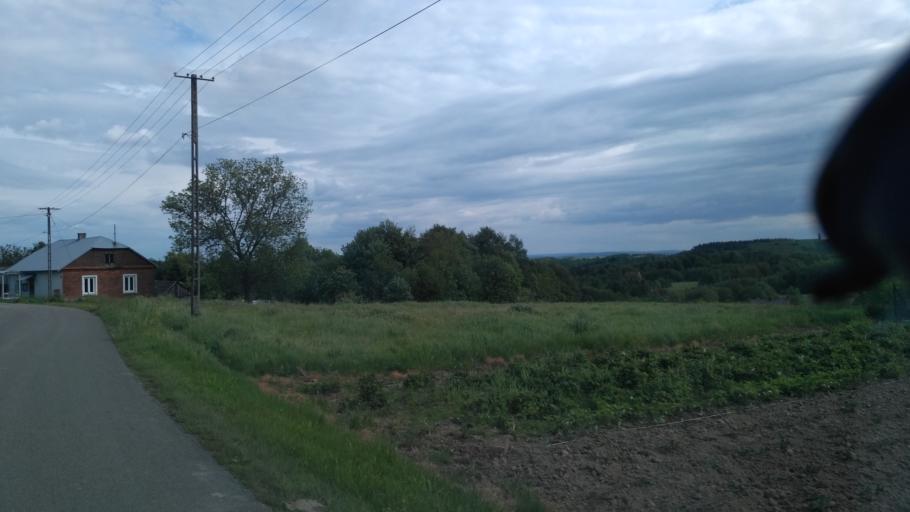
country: PL
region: Subcarpathian Voivodeship
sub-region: Powiat przeworski
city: Lopuszka Wielka
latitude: 49.8871
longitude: 22.4047
